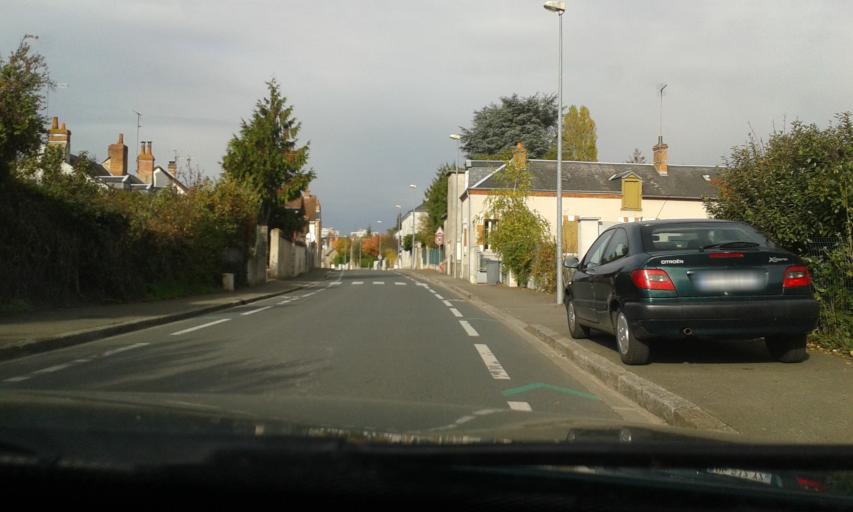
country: FR
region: Centre
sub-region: Departement du Loiret
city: Saint-Jean-le-Blanc
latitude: 47.8773
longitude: 1.9141
